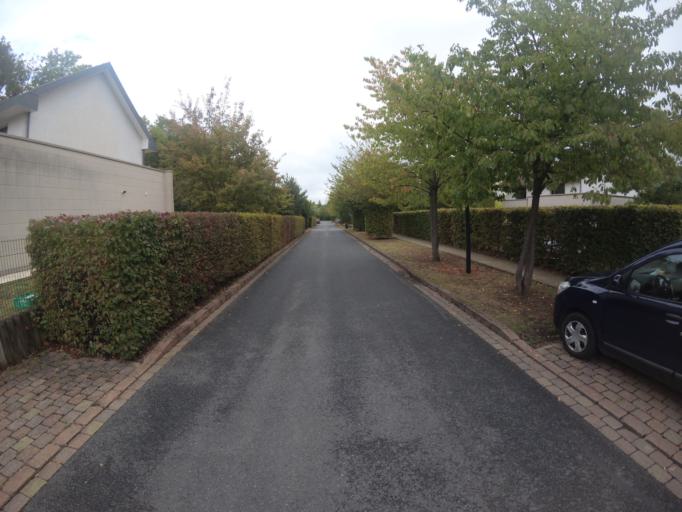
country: FR
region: Ile-de-France
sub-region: Departement de Seine-et-Marne
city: Montevrain
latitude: 48.8758
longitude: 2.7583
